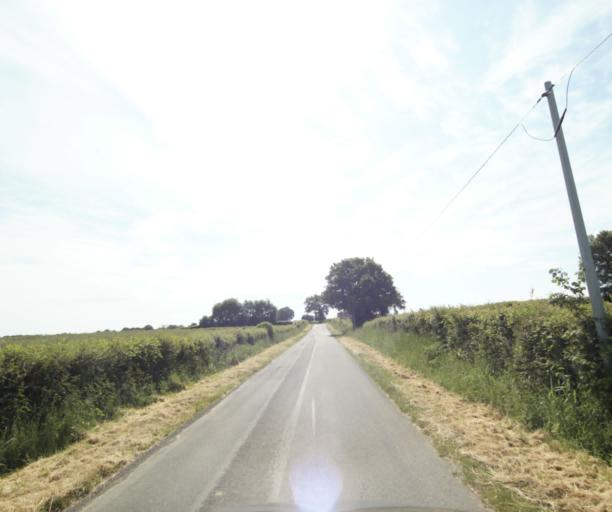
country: FR
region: Bourgogne
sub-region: Departement de Saone-et-Loire
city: Palinges
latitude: 46.5424
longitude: 4.1532
